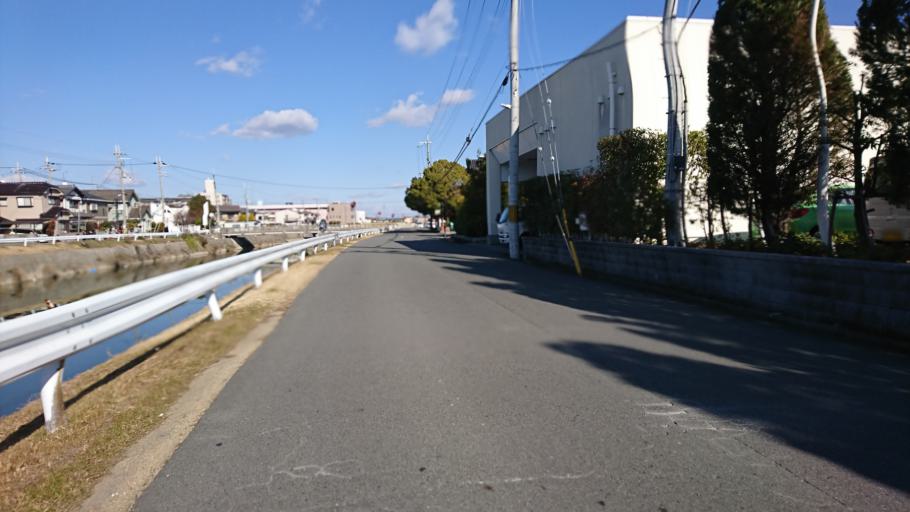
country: JP
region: Hyogo
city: Kakogawacho-honmachi
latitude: 34.7495
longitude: 134.8360
